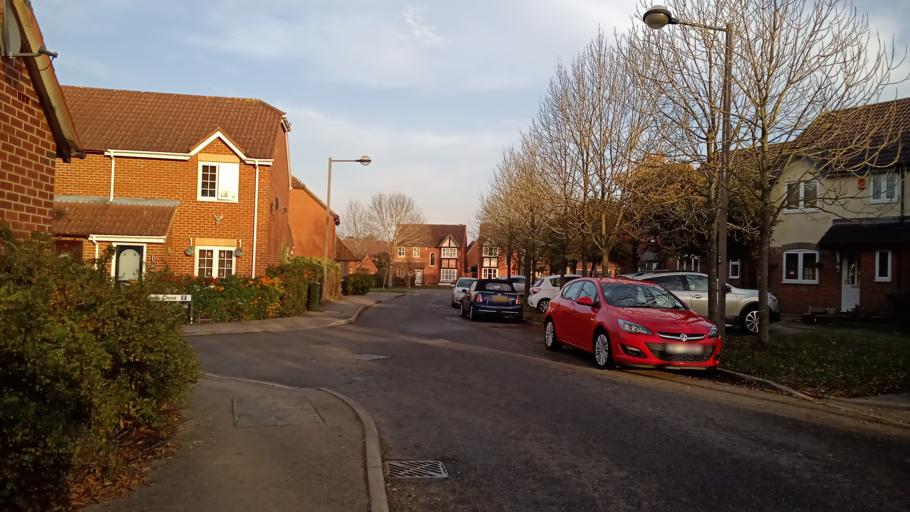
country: GB
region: England
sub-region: Milton Keynes
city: Shenley Church End
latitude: 52.0109
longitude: -0.7819
